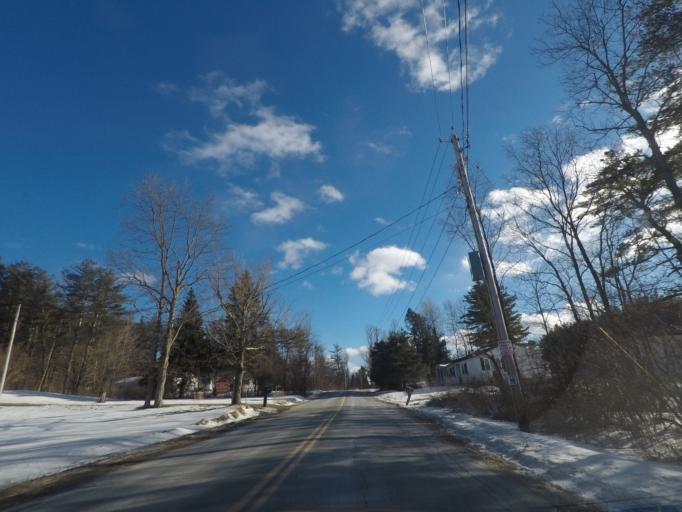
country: US
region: New York
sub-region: Rensselaer County
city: Hoosick Falls
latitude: 42.8428
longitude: -73.3936
